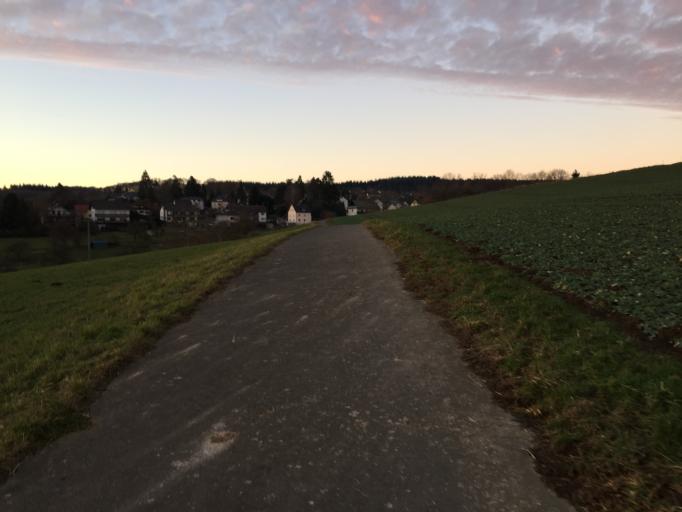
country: DE
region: Rheinland-Pfalz
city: Hardert
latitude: 50.5129
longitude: 7.5180
